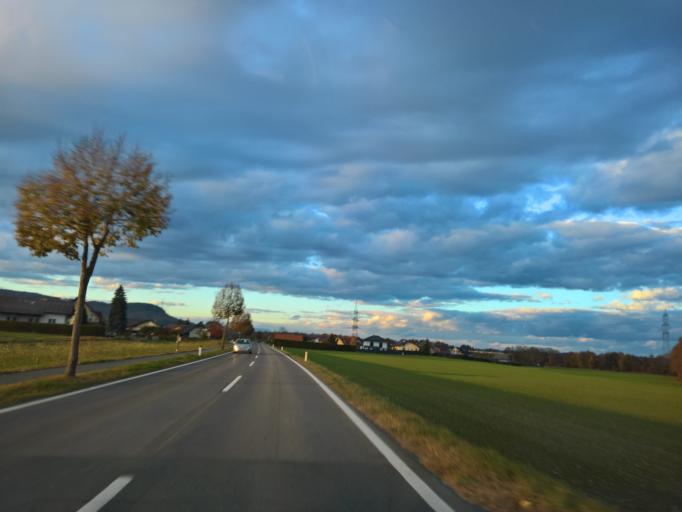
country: AT
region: Styria
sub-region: Politischer Bezirk Leibnitz
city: Kaindorf an der Sulm
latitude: 46.8313
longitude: 15.5433
